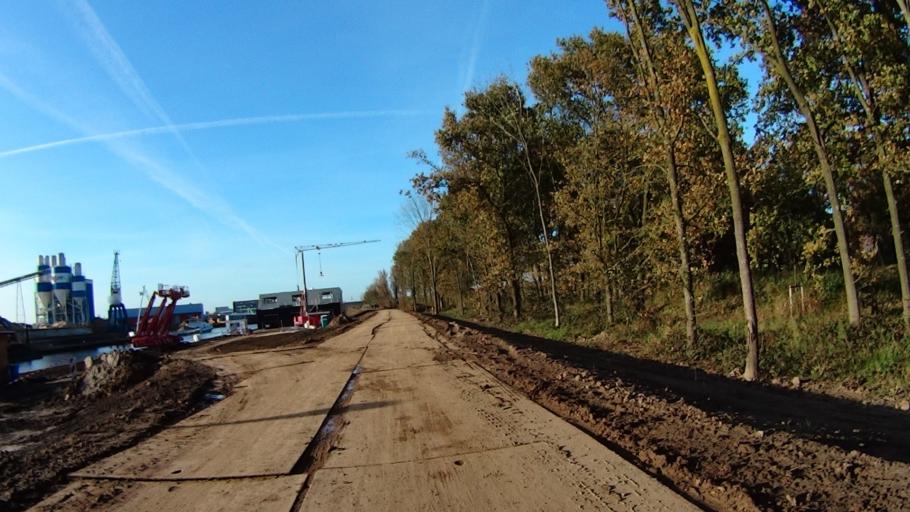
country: NL
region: Utrecht
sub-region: Gemeente Amersfoort
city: Hoogland
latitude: 52.1695
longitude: 5.3682
